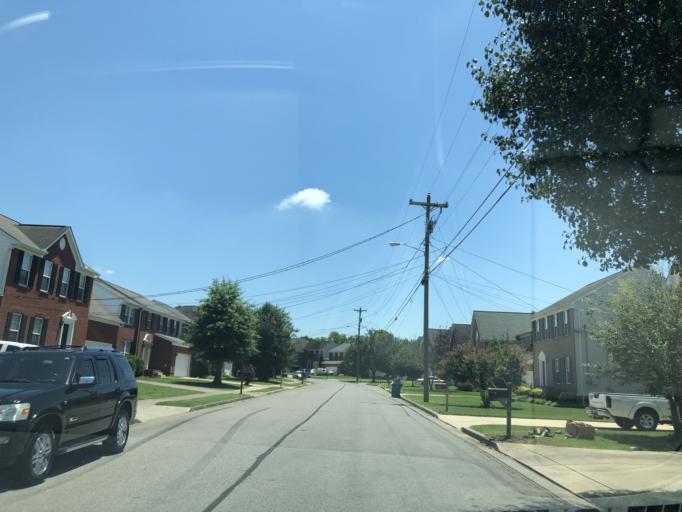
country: US
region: Tennessee
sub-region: Rutherford County
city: La Vergne
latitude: 36.0216
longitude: -86.6510
